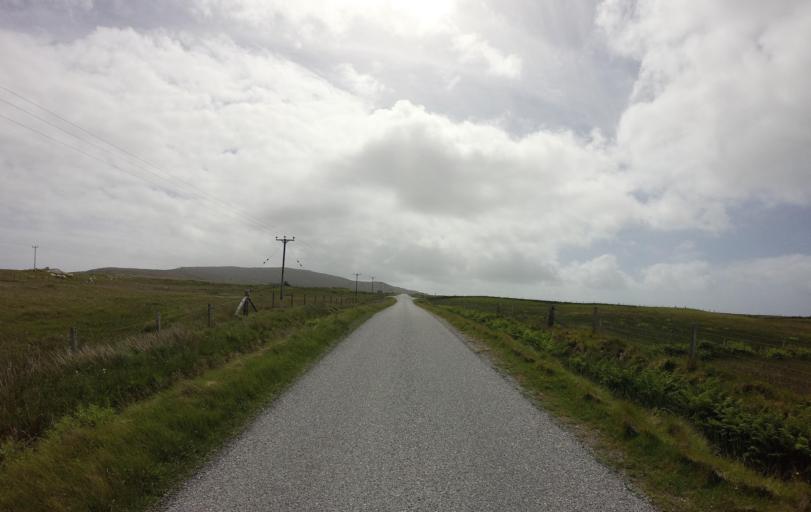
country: GB
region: Scotland
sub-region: Eilean Siar
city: Isle of South Uist
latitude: 57.1387
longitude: -7.3672
